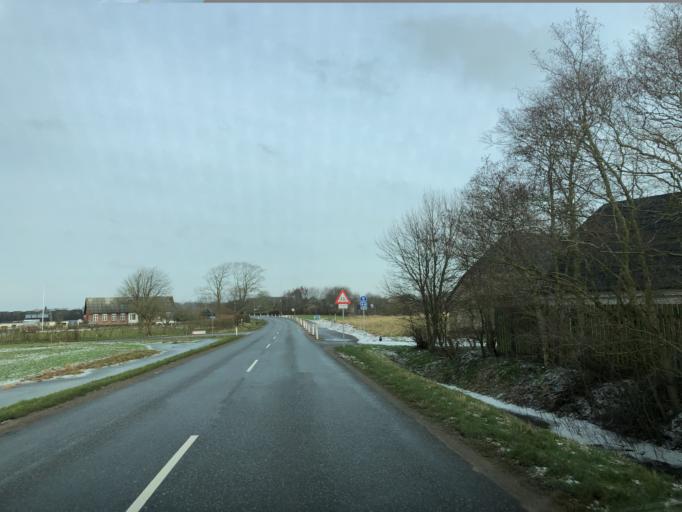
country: DK
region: South Denmark
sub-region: Vejle Kommune
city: Jelling
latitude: 55.8005
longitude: 9.4542
